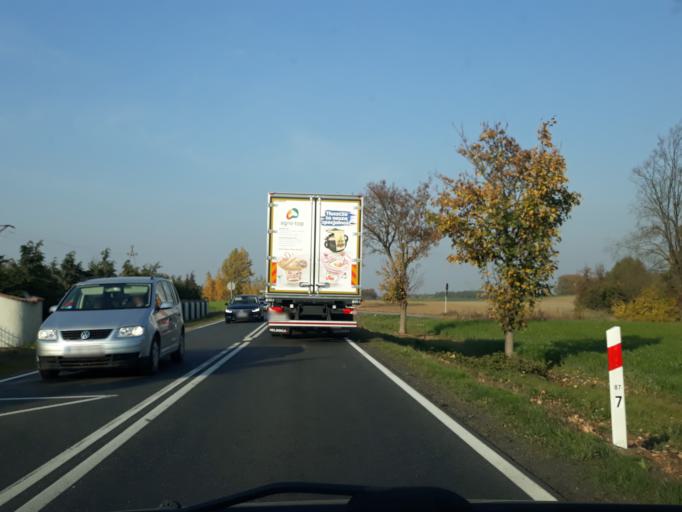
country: PL
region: Kujawsko-Pomorskie
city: Kamien Krajenski
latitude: 53.5014
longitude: 17.5071
